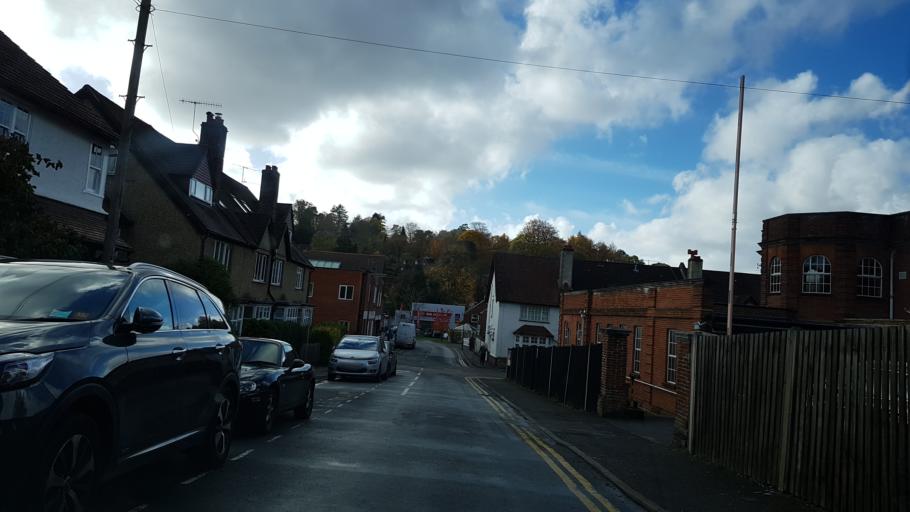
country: GB
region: England
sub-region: Surrey
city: Haslemere
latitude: 51.0904
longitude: -0.7104
